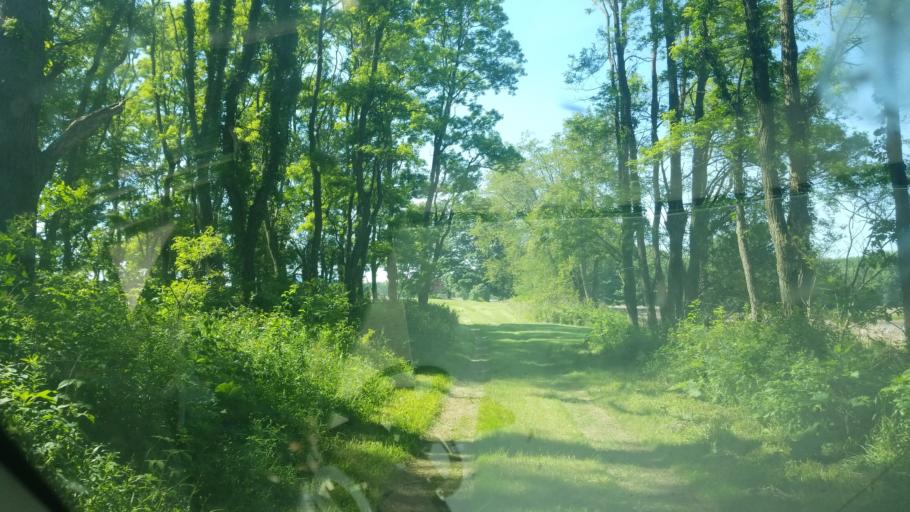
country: US
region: Ohio
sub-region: Morrow County
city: Mount Gilead
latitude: 40.5973
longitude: -82.7821
